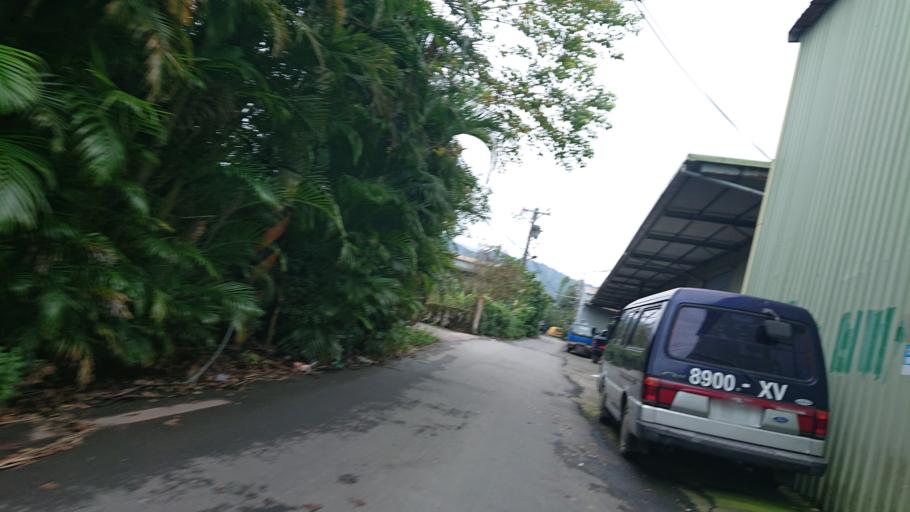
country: TW
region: Taiwan
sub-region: Taoyuan
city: Taoyuan
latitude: 24.9426
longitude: 121.3884
